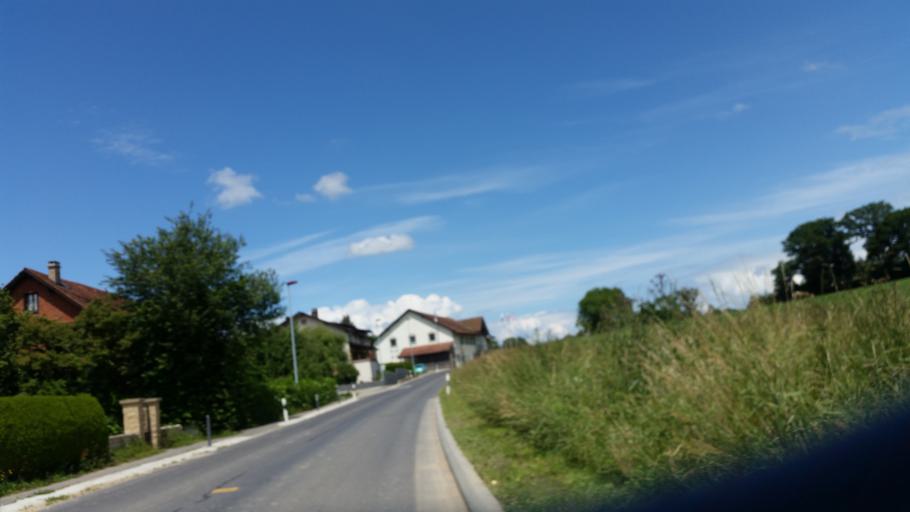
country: CH
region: Vaud
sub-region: Gros-de-Vaud District
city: Penthereaz
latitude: 46.6851
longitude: 6.6047
